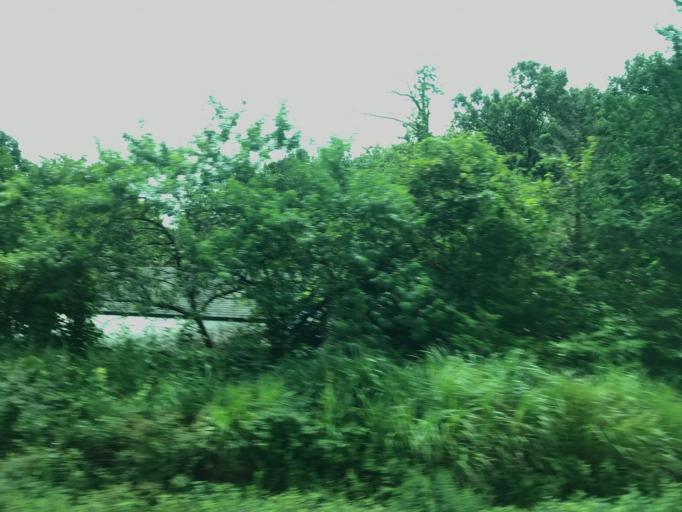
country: JP
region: Tochigi
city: Kuroiso
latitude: 36.9906
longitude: 140.0839
